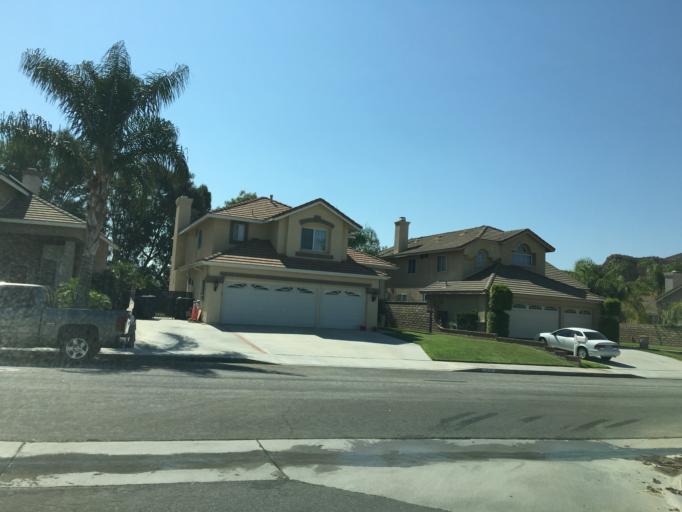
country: US
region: California
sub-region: Los Angeles County
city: Castaic
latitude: 34.4729
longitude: -118.6273
